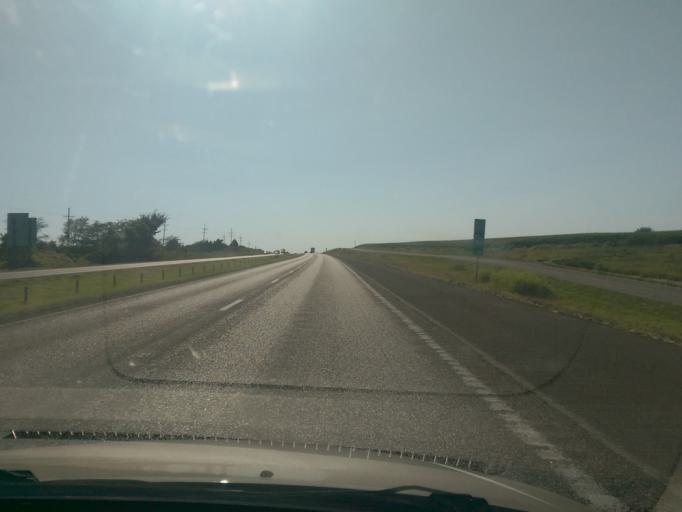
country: US
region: Missouri
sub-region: Lafayette County
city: Concordia
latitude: 38.9876
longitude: -93.5117
